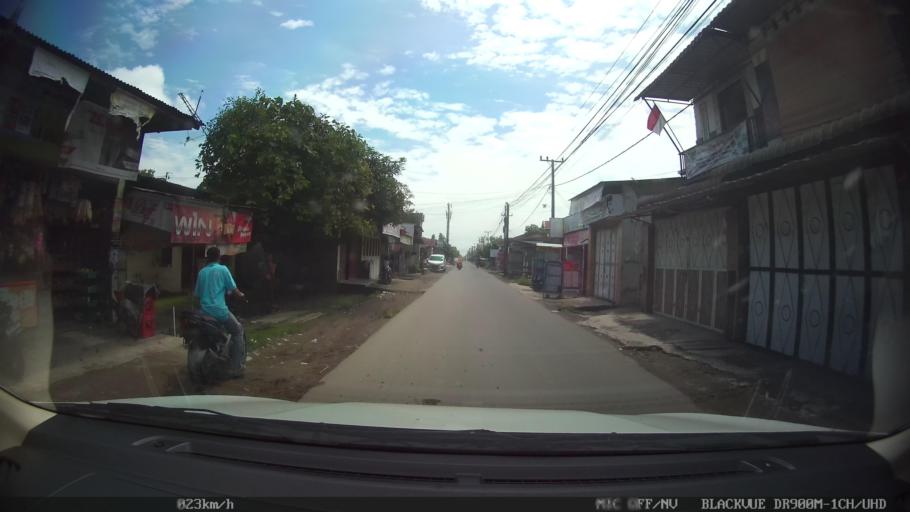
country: ID
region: North Sumatra
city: Medan
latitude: 3.5910
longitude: 98.7426
